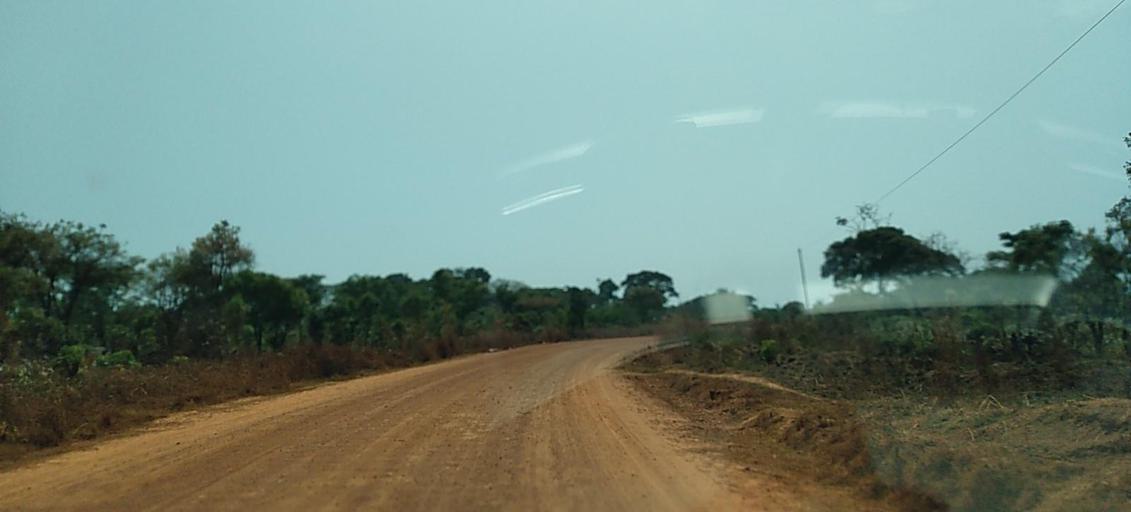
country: ZM
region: North-Western
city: Kansanshi
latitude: -11.9968
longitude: 26.5972
